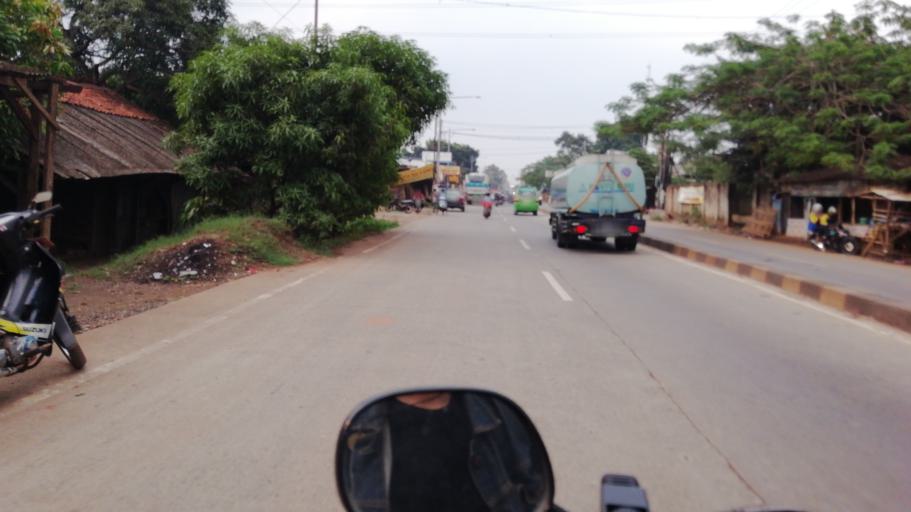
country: ID
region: West Java
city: Parung
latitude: -6.4484
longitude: 106.7318
